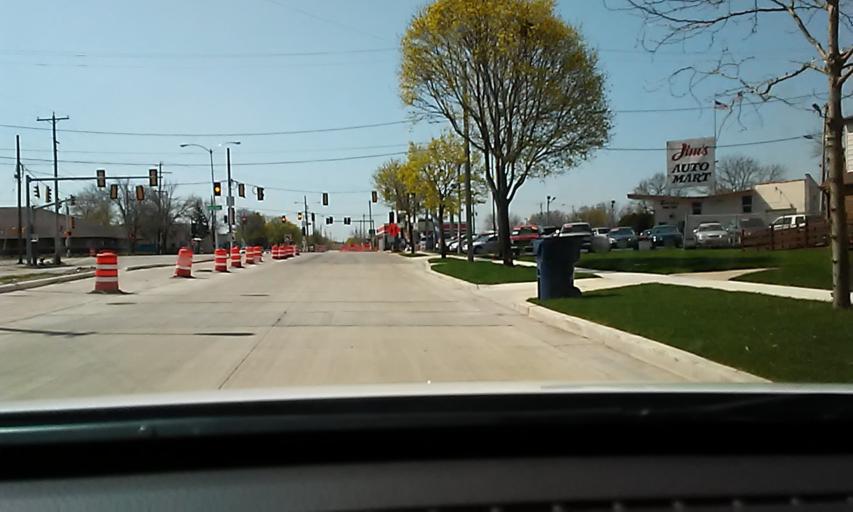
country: US
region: Wisconsin
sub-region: Milwaukee County
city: Greenfield
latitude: 42.9779
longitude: -87.9880
